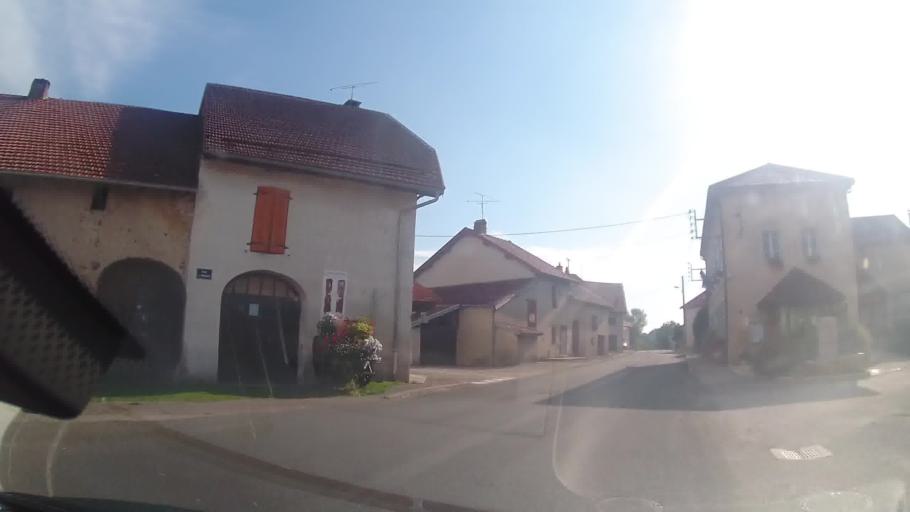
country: FR
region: Franche-Comte
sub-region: Departement du Jura
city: Clairvaux-les-Lacs
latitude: 46.5810
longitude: 5.7584
